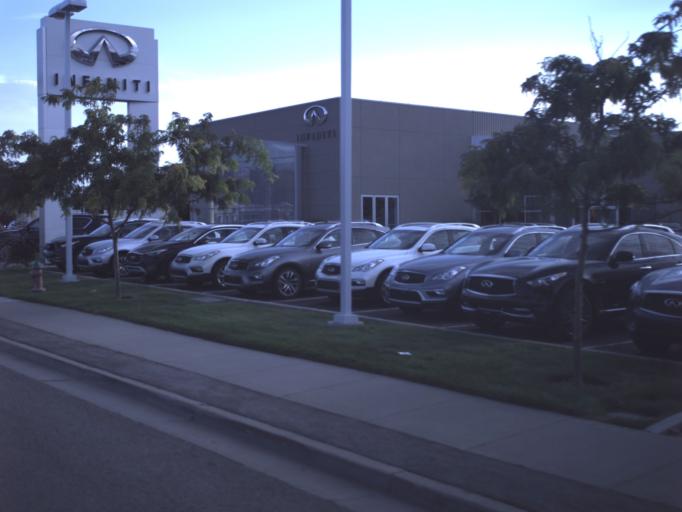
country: US
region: Utah
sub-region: Salt Lake County
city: Murray
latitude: 40.6726
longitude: -111.8884
